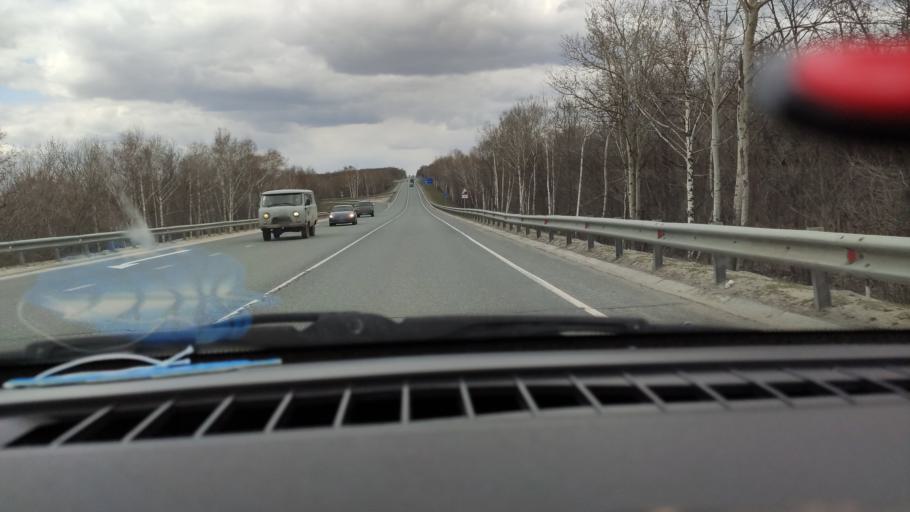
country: RU
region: Saratov
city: Vol'sk
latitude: 52.1091
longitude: 47.3776
